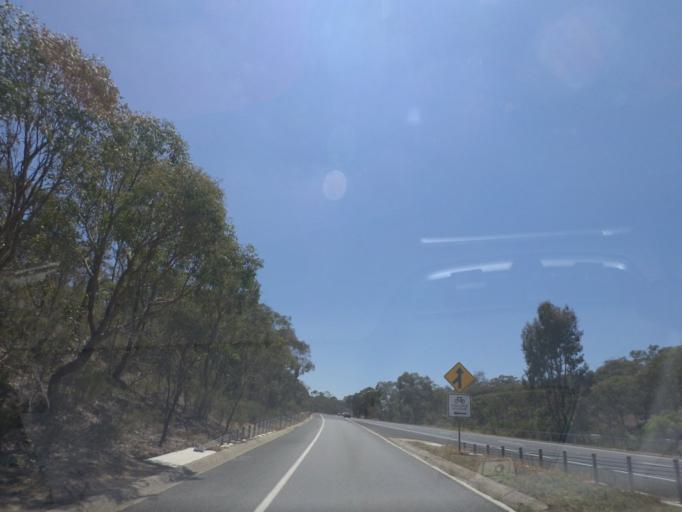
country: AU
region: Victoria
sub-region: Murrindindi
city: Kinglake West
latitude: -36.9618
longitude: 145.1833
